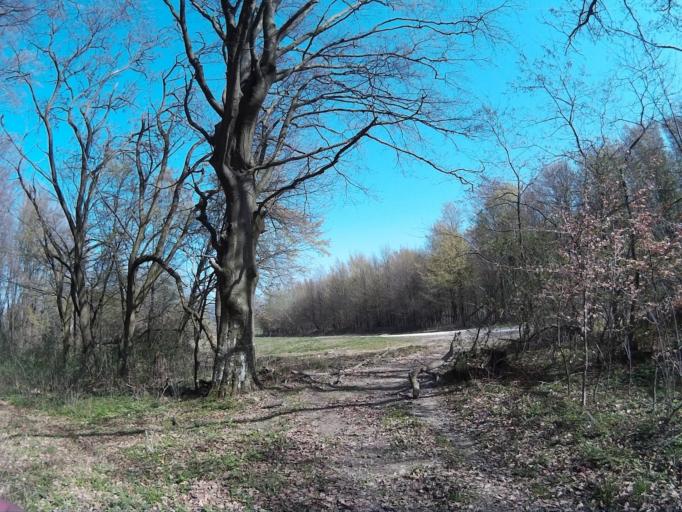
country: HU
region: Veszprem
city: Herend
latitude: 47.2079
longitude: 17.7911
